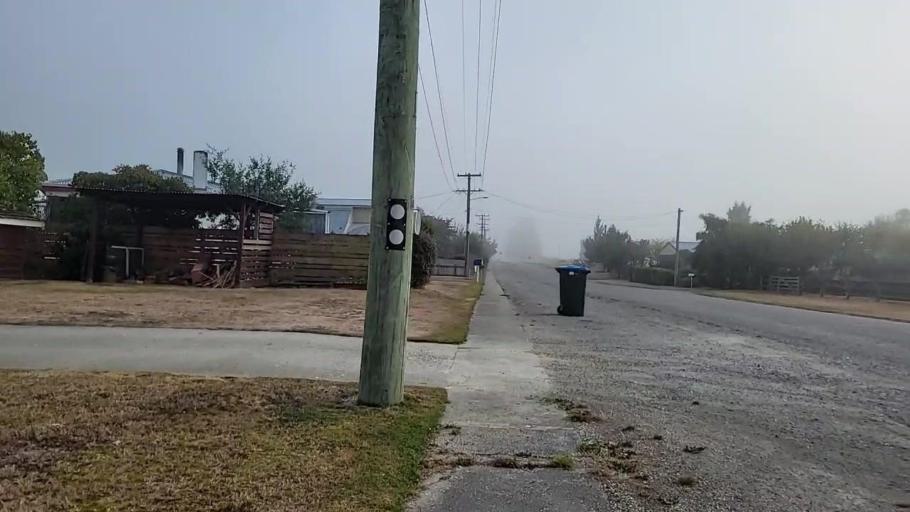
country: NZ
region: Southland
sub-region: Gore District
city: Gore
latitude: -45.6323
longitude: 169.3616
